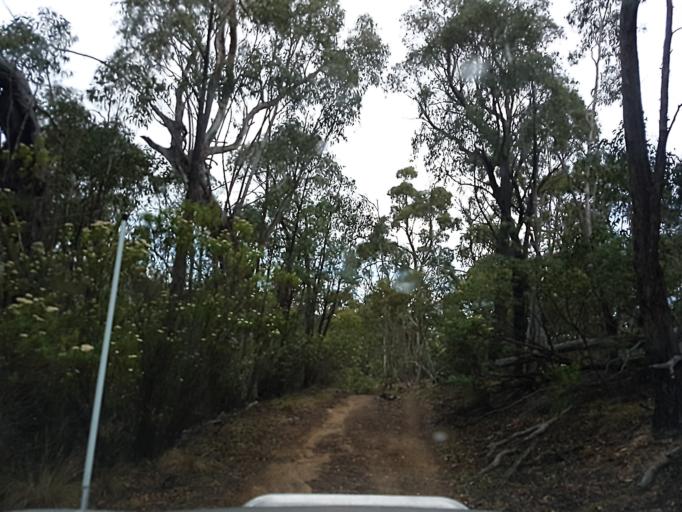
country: AU
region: New South Wales
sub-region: Snowy River
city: Jindabyne
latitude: -36.8891
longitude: 148.3374
